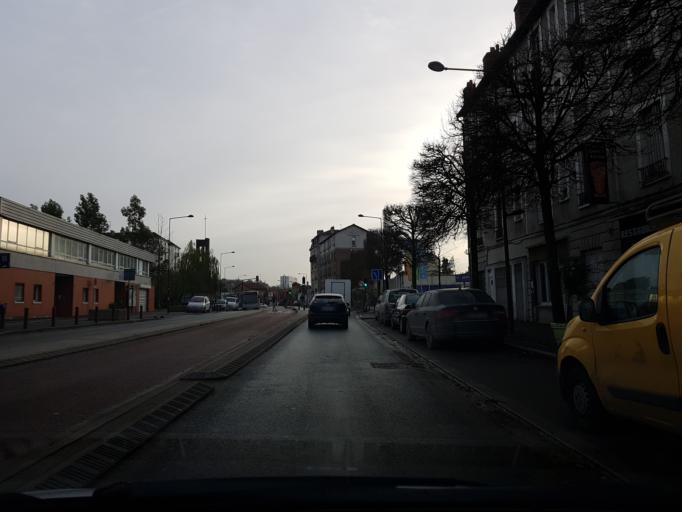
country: FR
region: Ile-de-France
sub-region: Departement du Val-de-Marne
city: Ablon-sur-Seine
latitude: 48.7279
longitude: 2.4357
